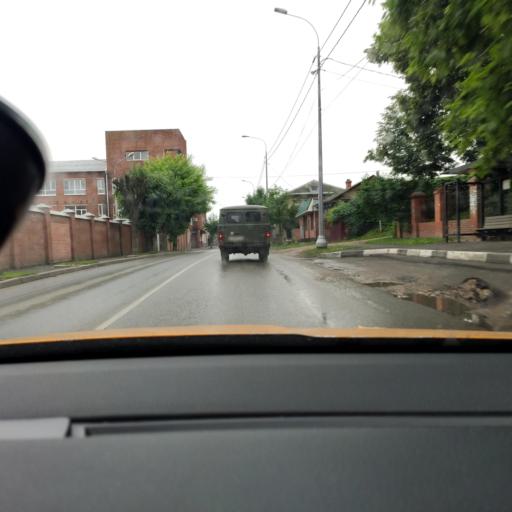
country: RU
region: Moskovskaya
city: Serpukhov
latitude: 54.9169
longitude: 37.3921
